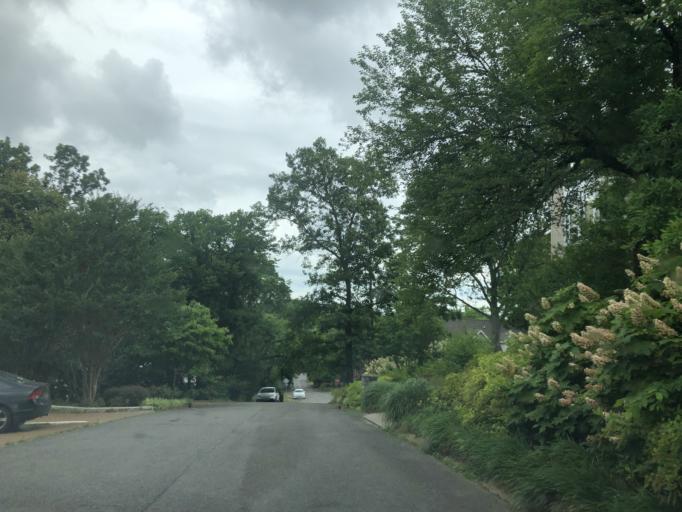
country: US
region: Tennessee
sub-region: Davidson County
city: Nashville
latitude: 36.1333
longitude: -86.8147
